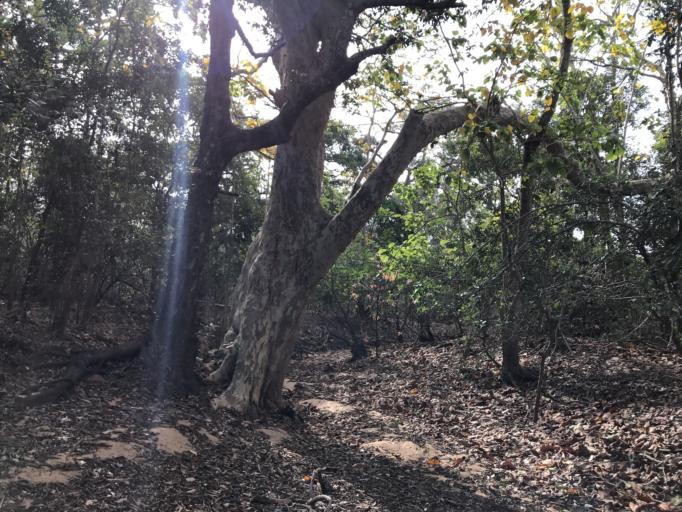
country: LK
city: Padaviya Divisional Secretariat
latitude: 9.0843
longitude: 80.8024
